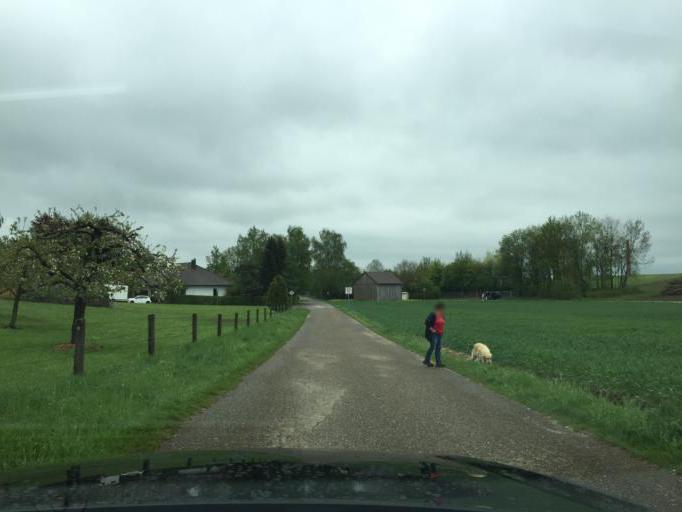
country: DE
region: Bavaria
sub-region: Swabia
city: Wertingen
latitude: 48.5652
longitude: 10.6672
